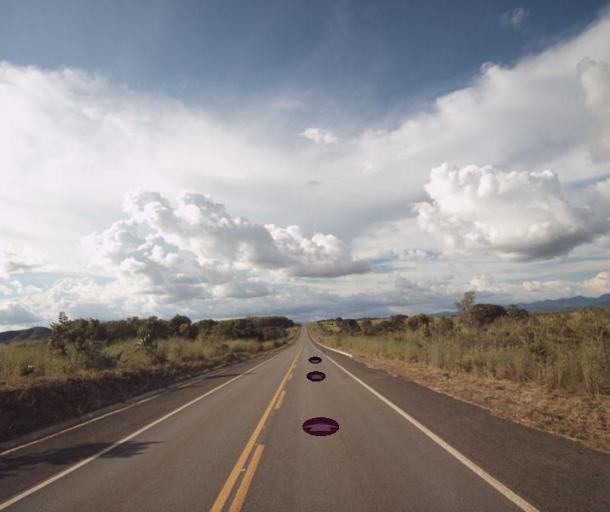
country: BR
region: Goias
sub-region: Barro Alto
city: Barro Alto
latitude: -14.8345
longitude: -48.6382
